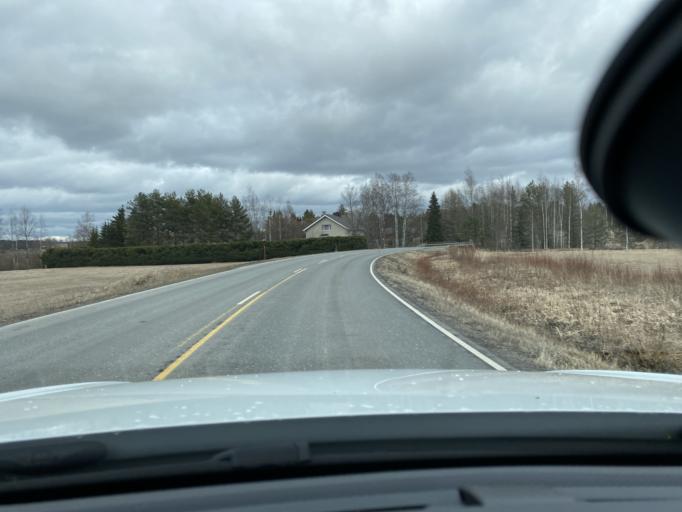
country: FI
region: Pirkanmaa
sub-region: Lounais-Pirkanmaa
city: Punkalaidun
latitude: 61.1045
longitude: 23.1864
